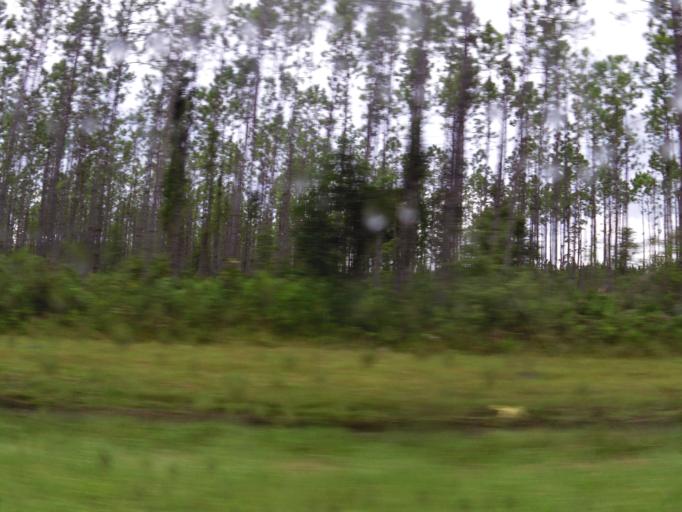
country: US
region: Florida
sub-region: Duval County
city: Baldwin
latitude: 30.4704
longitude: -81.9977
